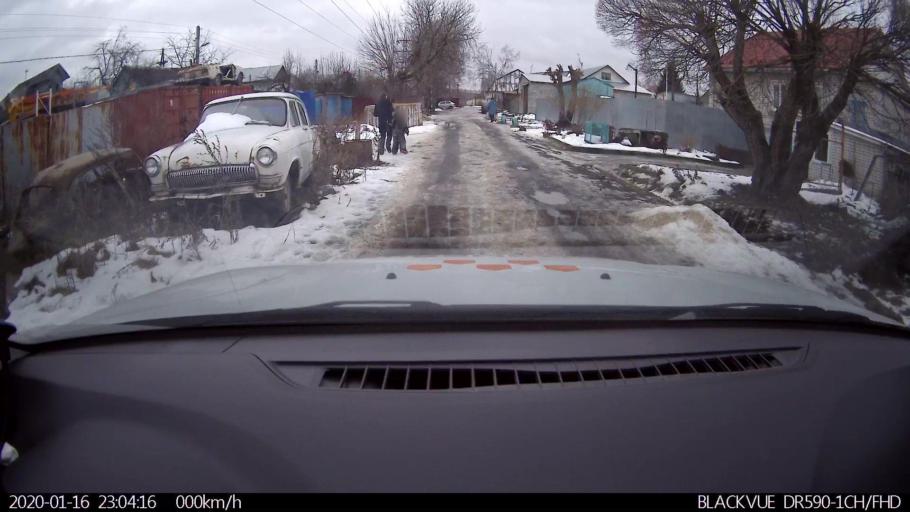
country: RU
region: Nizjnij Novgorod
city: Nizhniy Novgorod
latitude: 56.2840
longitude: 43.9035
